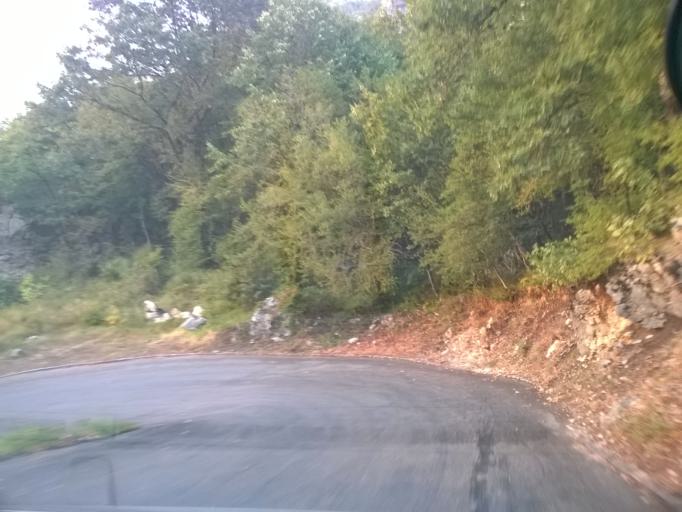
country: ME
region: Opstina Niksic
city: Niksic
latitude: 42.6728
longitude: 19.0296
